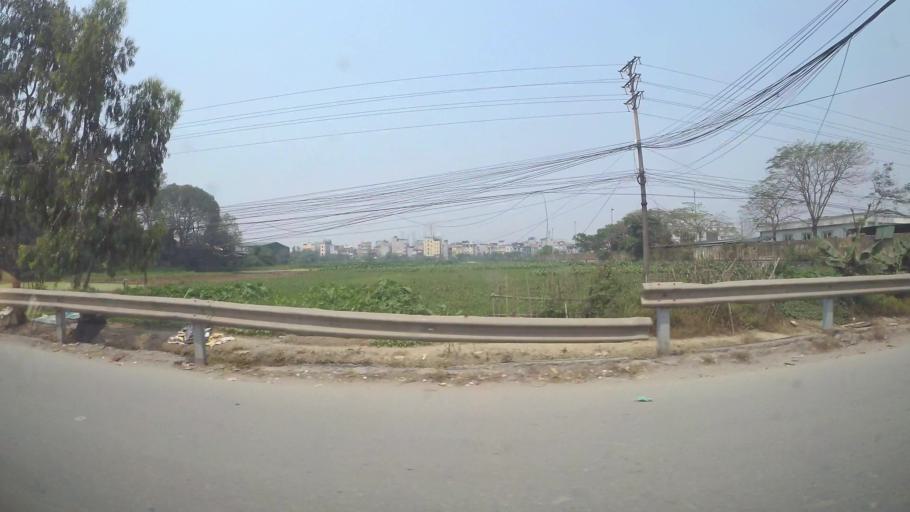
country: VN
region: Ha Noi
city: Van Dien
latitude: 20.9550
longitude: 105.8119
